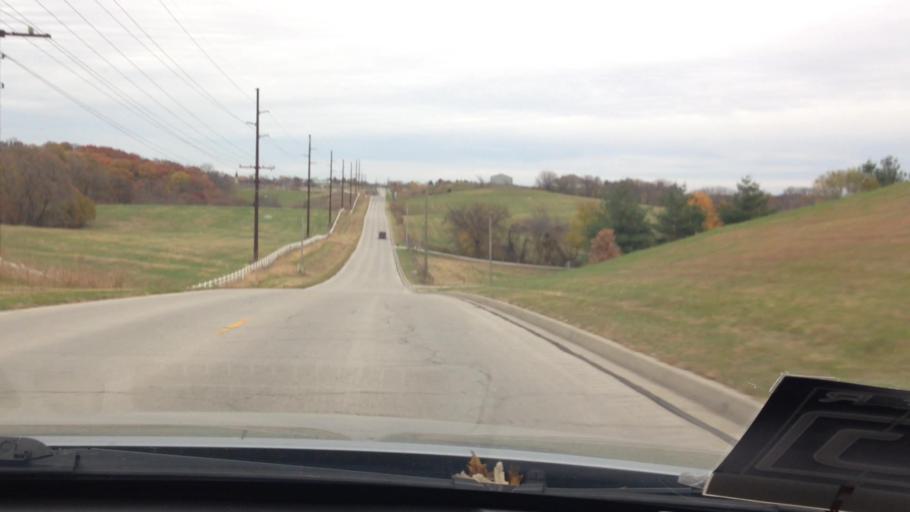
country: US
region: Missouri
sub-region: Platte County
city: Platte City
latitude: 39.3391
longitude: -94.8004
